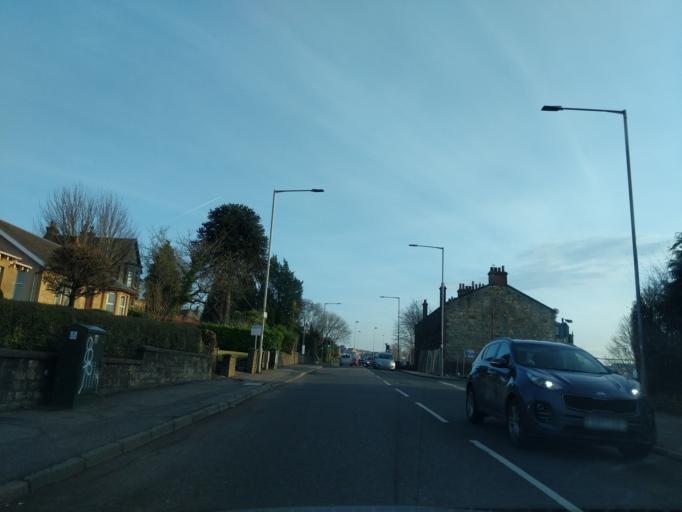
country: GB
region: Scotland
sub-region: South Lanarkshire
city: Carluke
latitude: 55.7302
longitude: -3.8369
